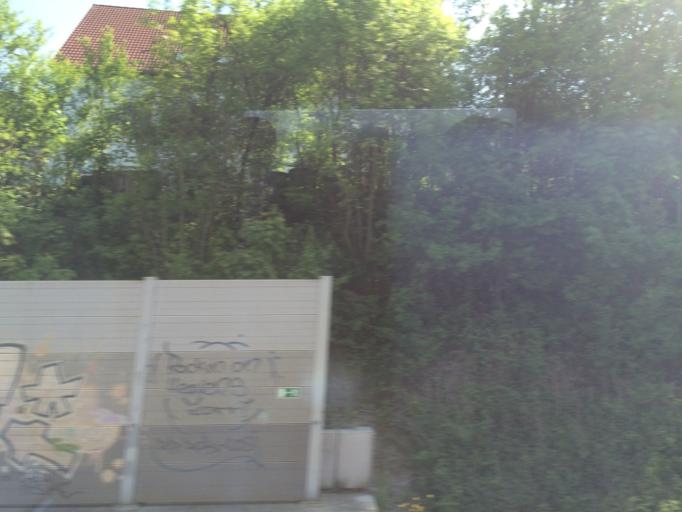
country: DE
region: Bavaria
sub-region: Regierungsbezirk Mittelfranken
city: Neustadt an der Aisch
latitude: 49.5737
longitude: 10.6046
